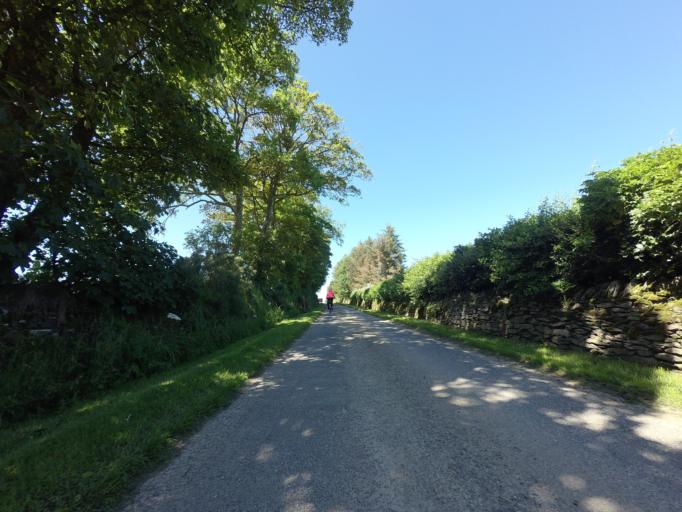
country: GB
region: Scotland
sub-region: Aberdeenshire
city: Macduff
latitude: 57.6379
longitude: -2.4939
